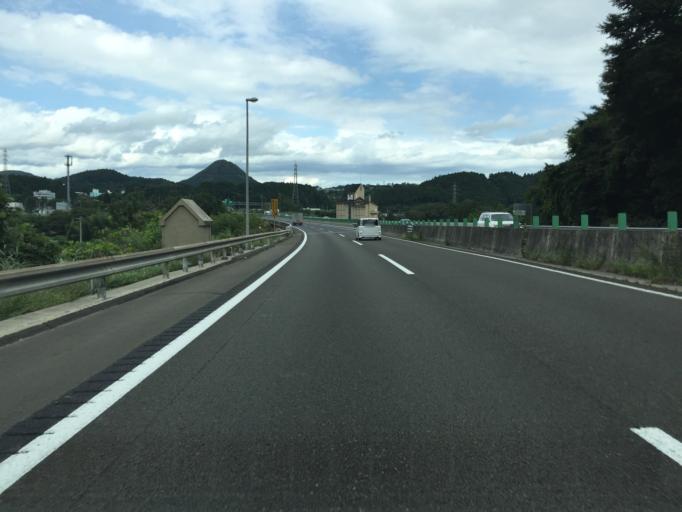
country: JP
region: Miyagi
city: Sendai
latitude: 38.2095
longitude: 140.8047
